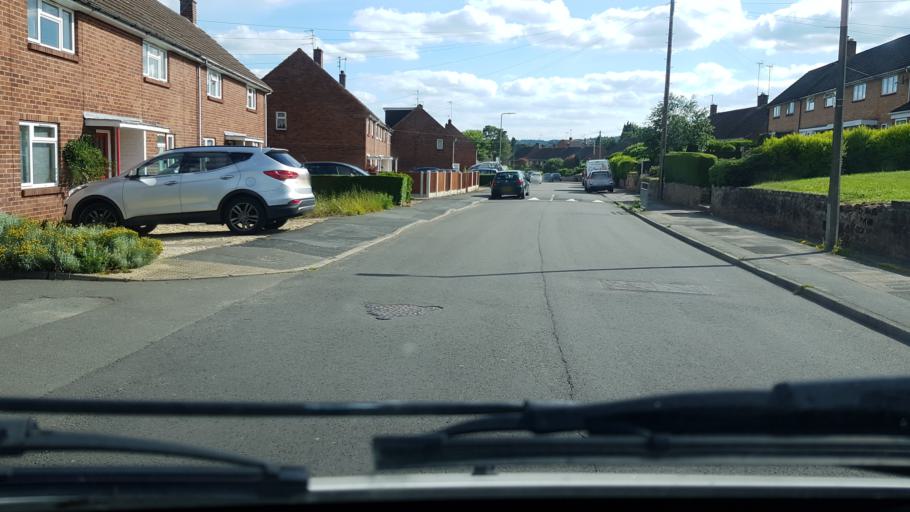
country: GB
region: England
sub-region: Worcestershire
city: Bewdley
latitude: 52.3824
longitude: -2.3042
